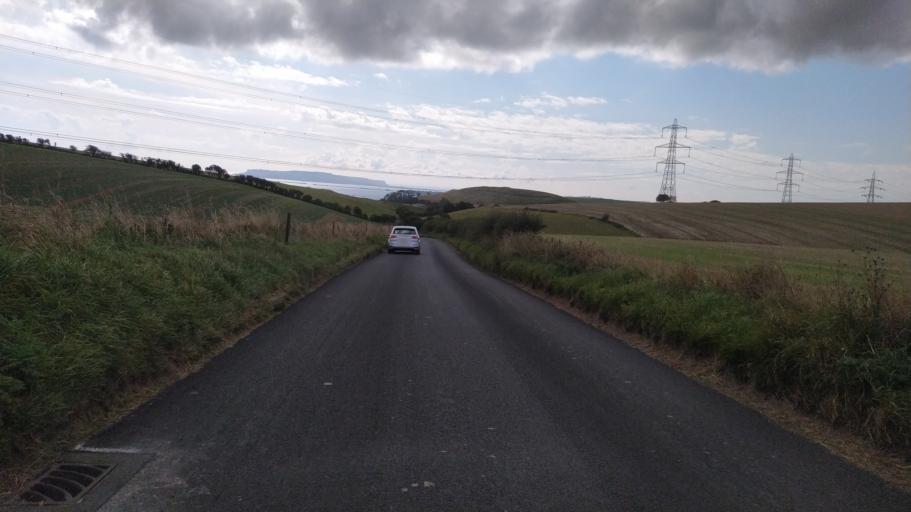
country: GB
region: England
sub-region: Dorset
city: Overcombe
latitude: 50.6632
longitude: -2.4281
